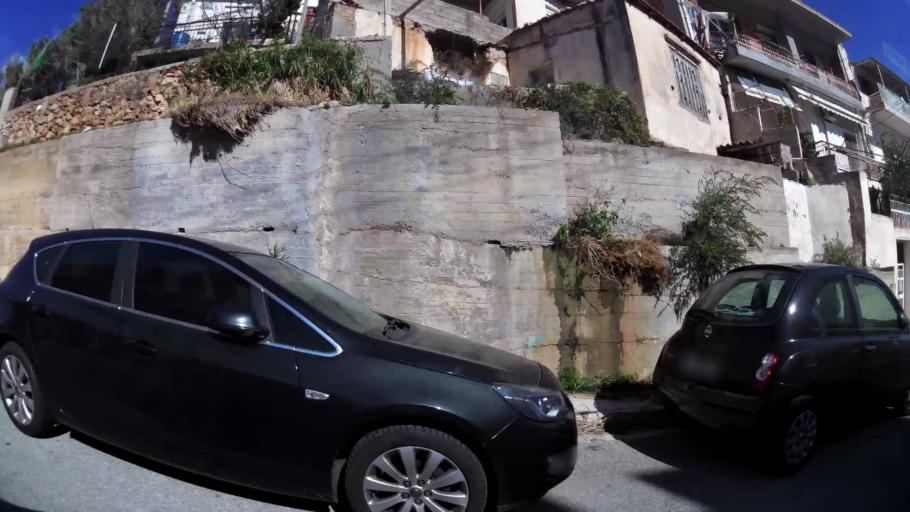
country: GR
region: Attica
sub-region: Nomos Piraios
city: Perama
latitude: 37.9692
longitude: 23.5690
